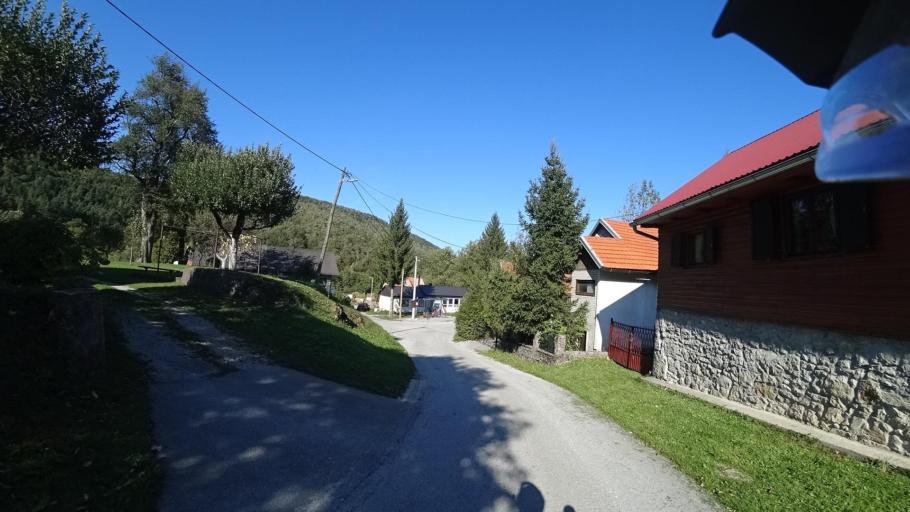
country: HR
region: Karlovacka
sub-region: Grad Ogulin
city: Ogulin
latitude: 45.2902
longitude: 15.1446
